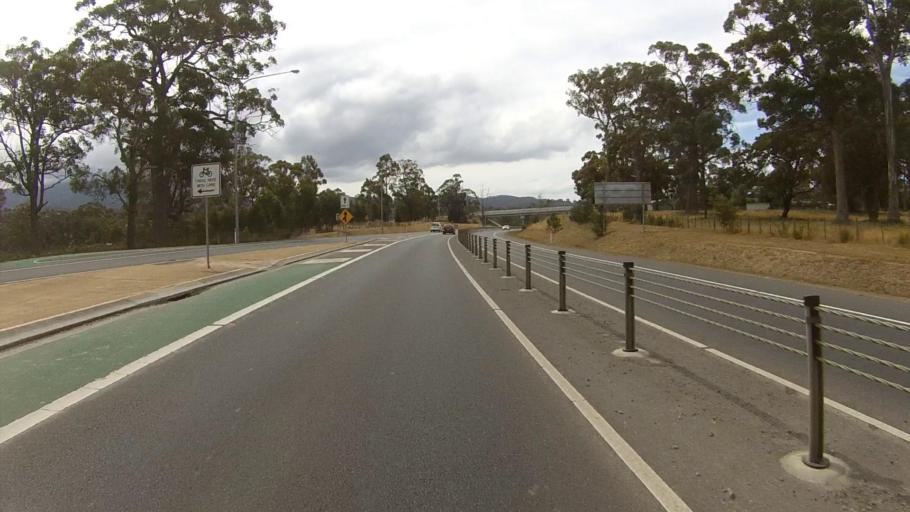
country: AU
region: Tasmania
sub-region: Kingborough
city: Kingston
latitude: -42.9855
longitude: 147.2890
